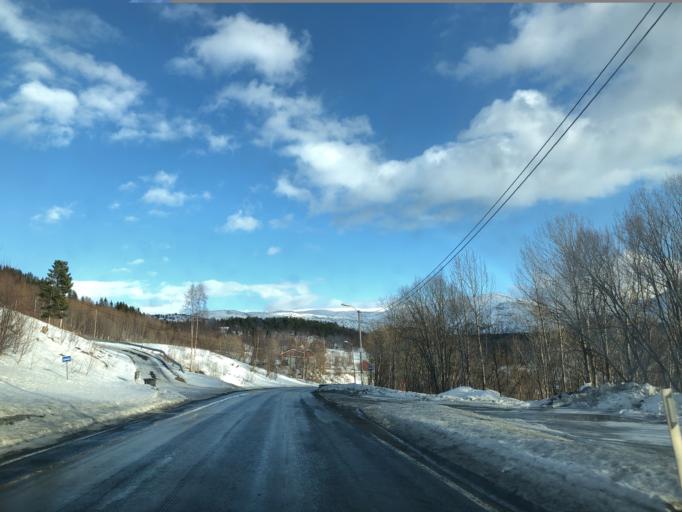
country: NO
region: Nordland
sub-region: Narvik
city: Bjerkvik
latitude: 68.4640
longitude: 17.6822
